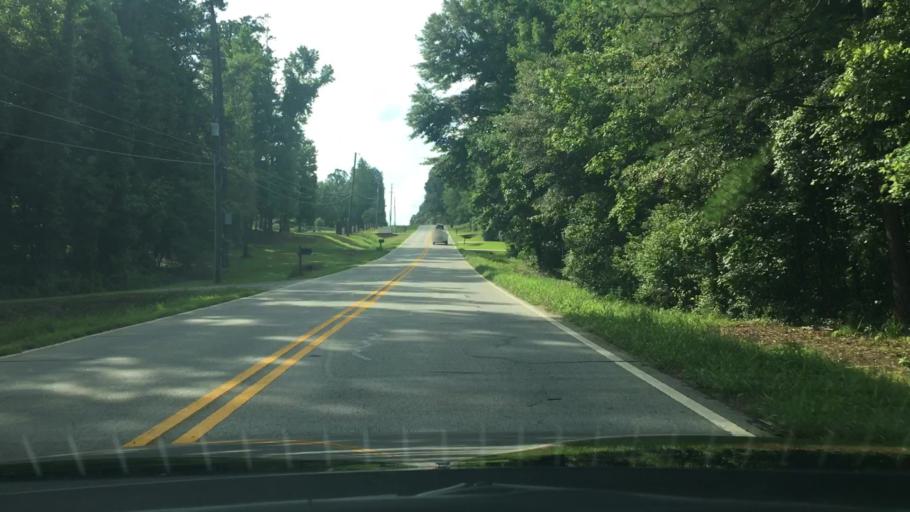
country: US
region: Georgia
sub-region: Coweta County
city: East Newnan
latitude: 33.3502
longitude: -84.6980
